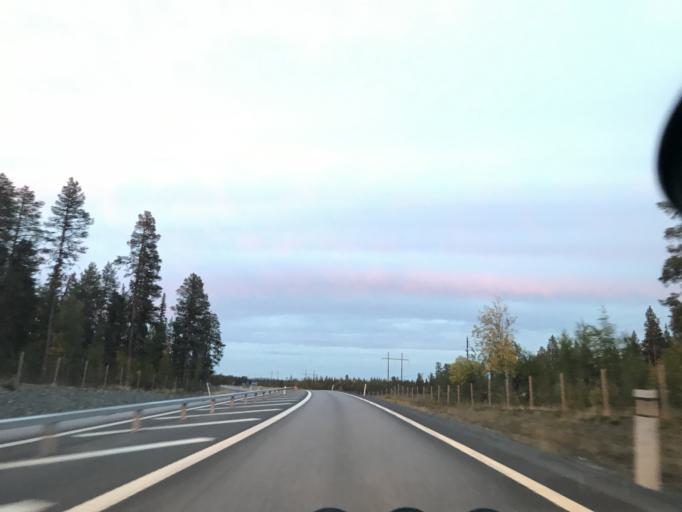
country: SE
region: Norrbotten
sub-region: Gallivare Kommun
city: Malmberget
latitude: 67.6724
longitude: 20.9162
